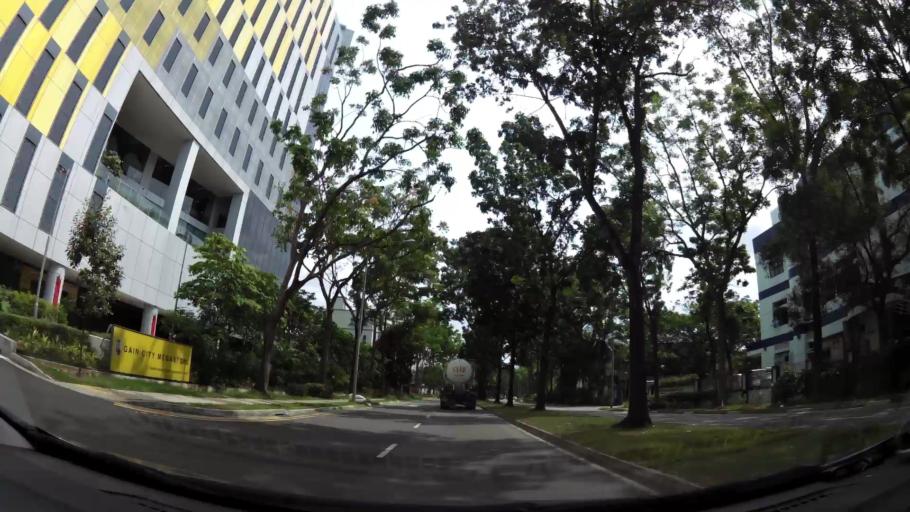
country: MY
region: Johor
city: Johor Bahru
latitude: 1.4130
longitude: 103.7453
